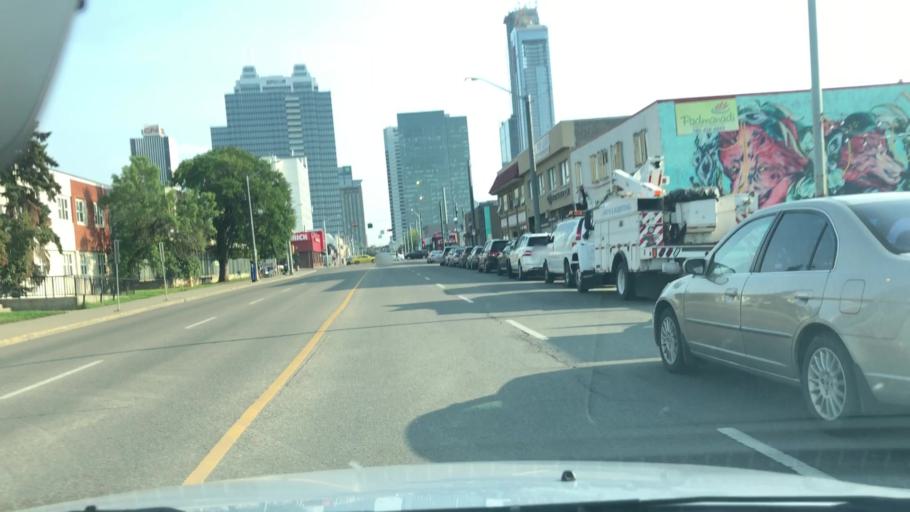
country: CA
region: Alberta
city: Edmonton
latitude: 53.5528
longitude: -113.4937
